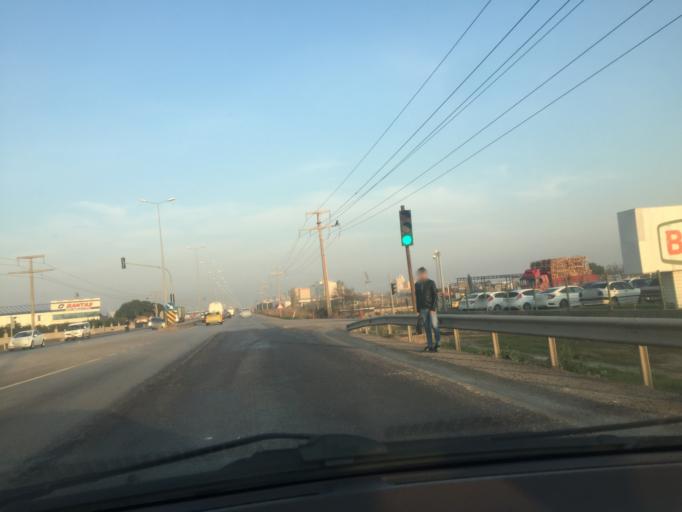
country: TR
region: Balikesir
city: Bandirma
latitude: 40.2934
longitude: 28.0367
